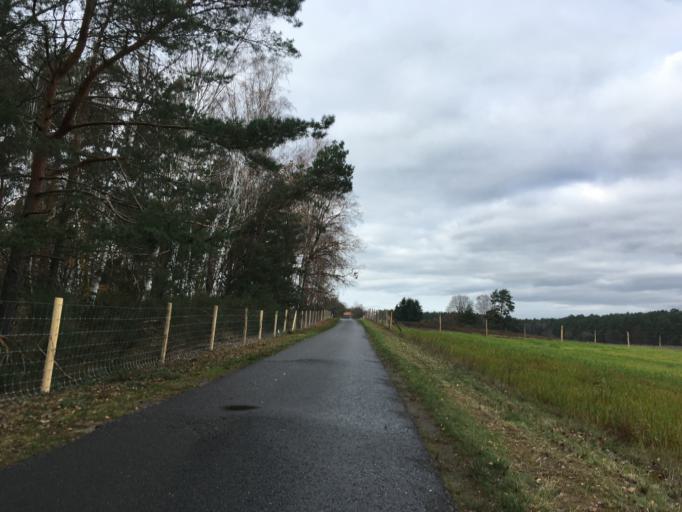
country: DE
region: Brandenburg
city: Jamlitz
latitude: 52.0259
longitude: 14.4719
